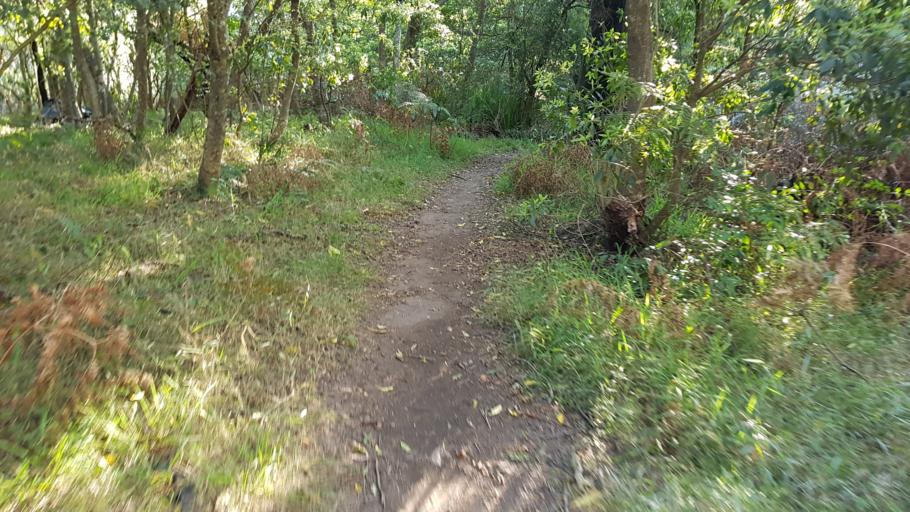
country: AU
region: New South Wales
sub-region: Willoughby
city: Chatswood West
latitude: -33.7990
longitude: 151.1506
